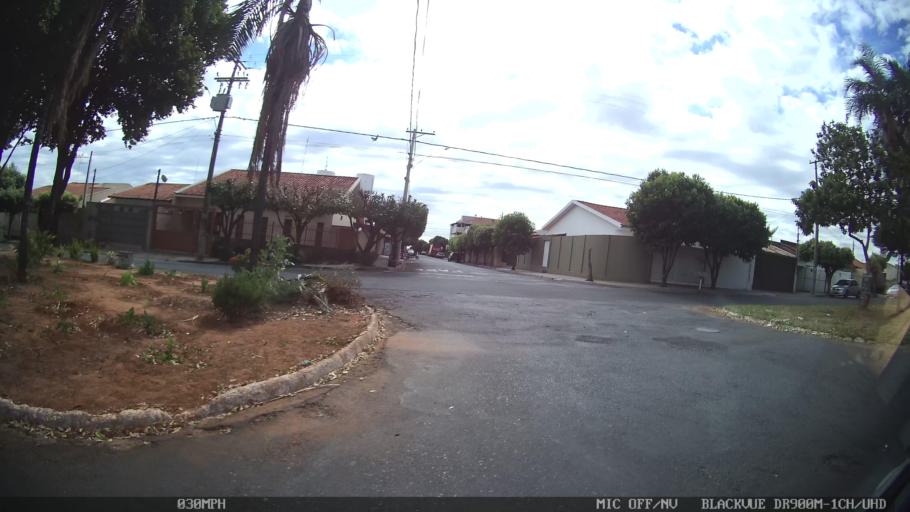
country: BR
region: Sao Paulo
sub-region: Sao Jose Do Rio Preto
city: Sao Jose do Rio Preto
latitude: -20.8083
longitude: -49.4948
